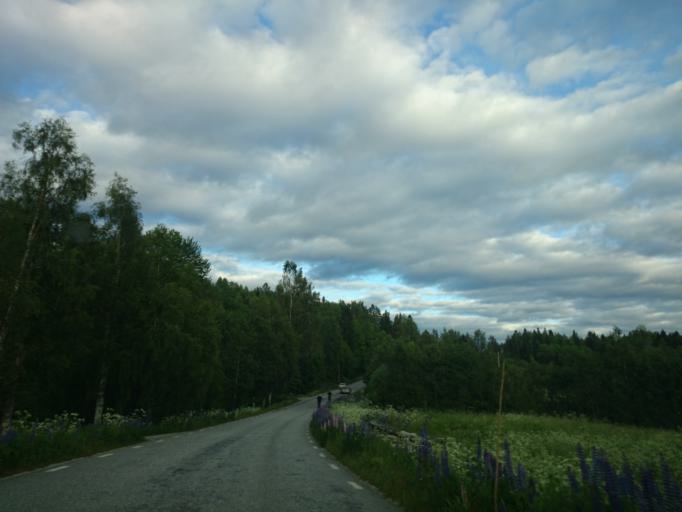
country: SE
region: Vaesternorrland
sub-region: Haernoesands Kommun
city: Haernoesand
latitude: 62.5821
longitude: 17.8138
